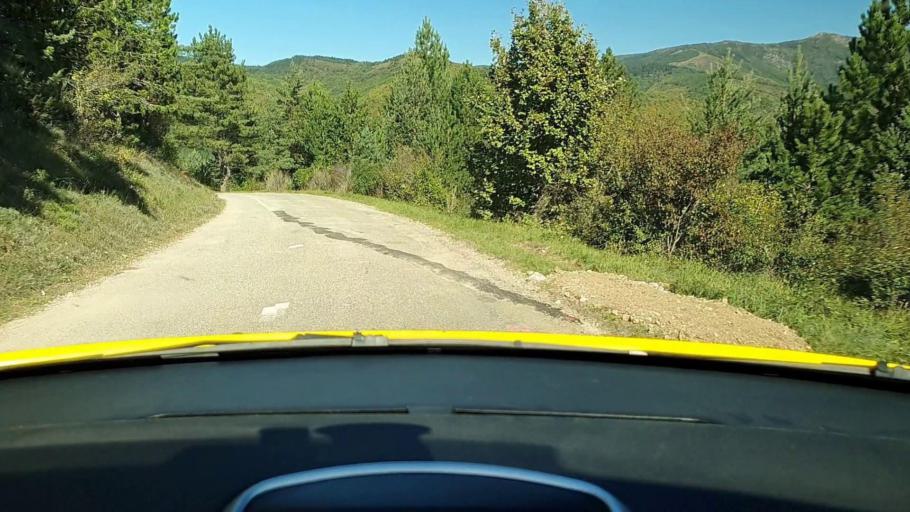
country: FR
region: Languedoc-Roussillon
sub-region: Departement du Gard
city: Aveze
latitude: 43.9612
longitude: 3.4336
